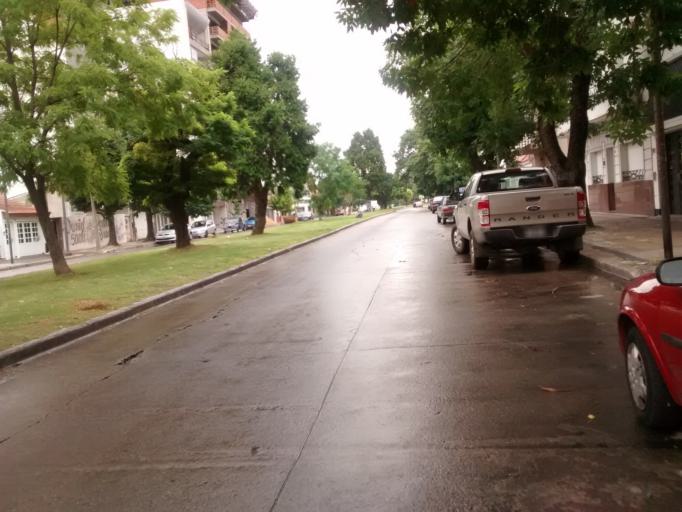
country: AR
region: Buenos Aires
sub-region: Partido de La Plata
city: La Plata
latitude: -34.9184
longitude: -57.9722
